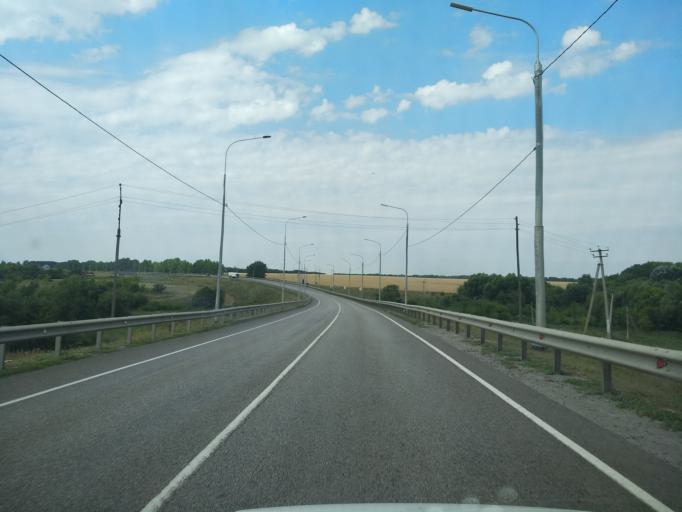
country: RU
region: Lipetsk
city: Dobrinka
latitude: 51.9140
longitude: 40.4630
